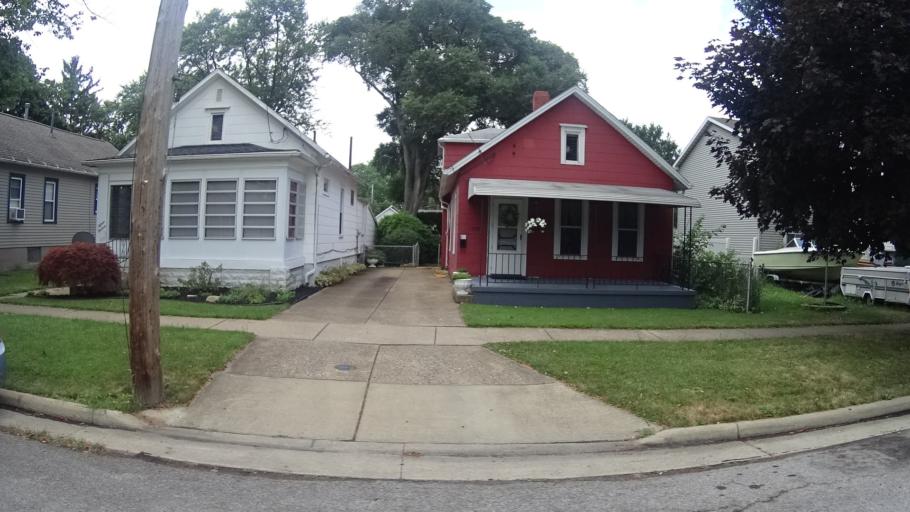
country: US
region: Ohio
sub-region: Erie County
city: Sandusky
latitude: 41.4424
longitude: -82.7216
